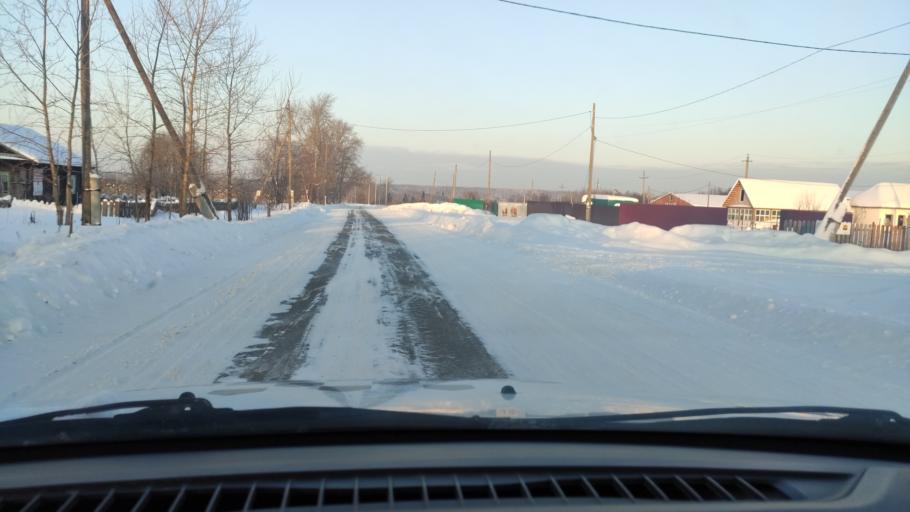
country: RU
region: Perm
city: Sylva
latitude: 58.0383
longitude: 56.7248
